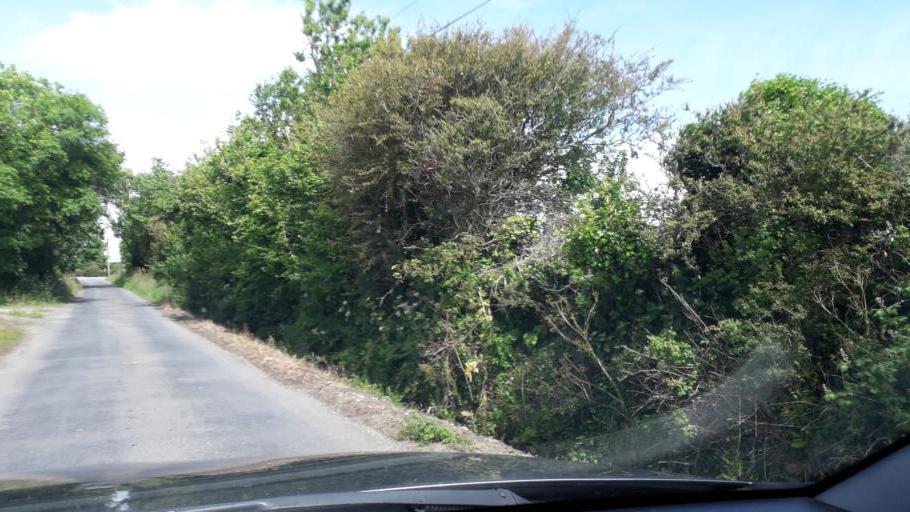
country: IE
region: Leinster
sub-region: Loch Garman
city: Loch Garman
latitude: 52.1923
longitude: -6.5466
